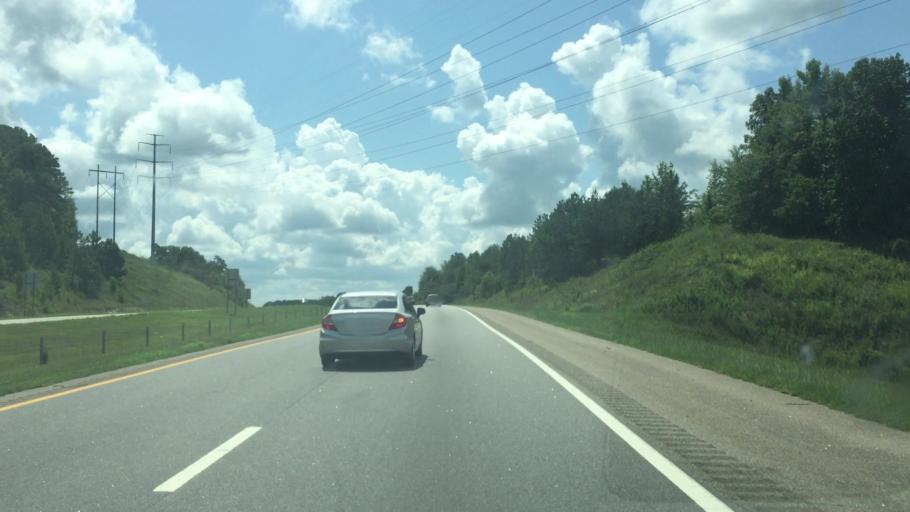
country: US
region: North Carolina
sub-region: Richmond County
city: Cordova
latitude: 34.9389
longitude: -79.8420
